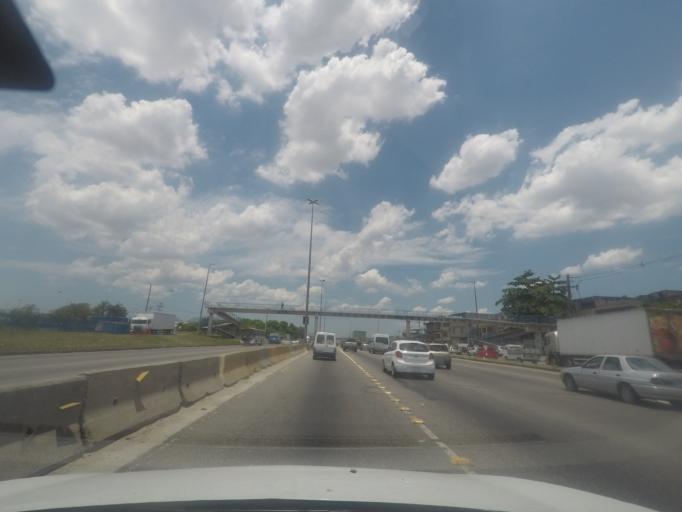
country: BR
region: Rio de Janeiro
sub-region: Sao Joao De Meriti
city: Sao Joao de Meriti
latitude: -22.8277
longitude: -43.3423
